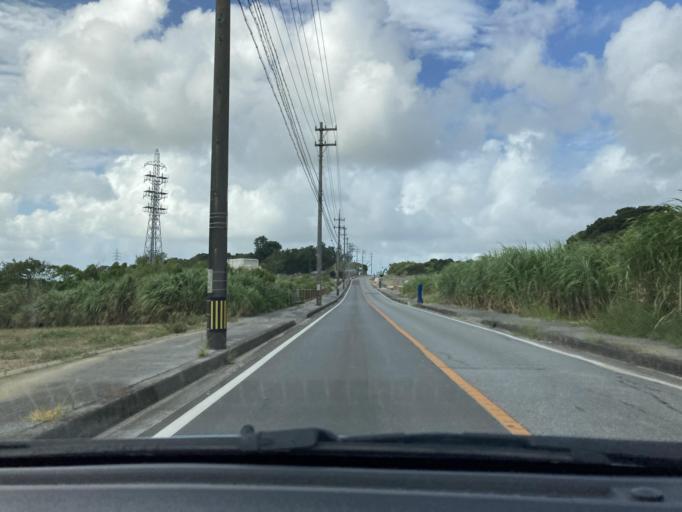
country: JP
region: Okinawa
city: Itoman
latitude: 26.1067
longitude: 127.6948
